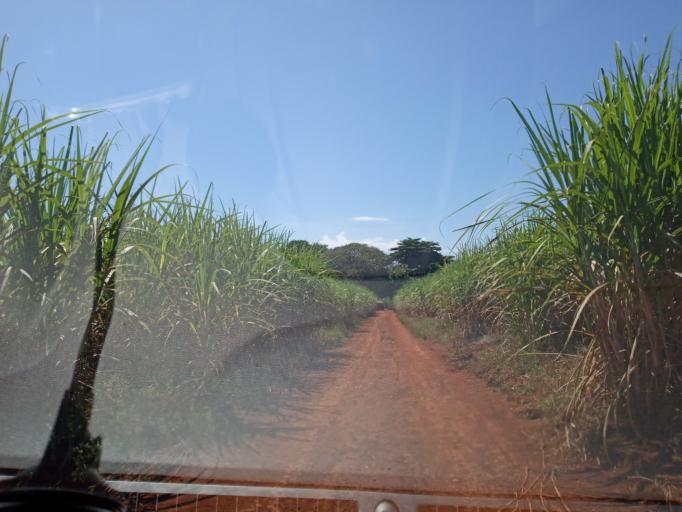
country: BR
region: Goias
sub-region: Itumbiara
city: Itumbiara
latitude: -18.4370
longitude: -49.1475
